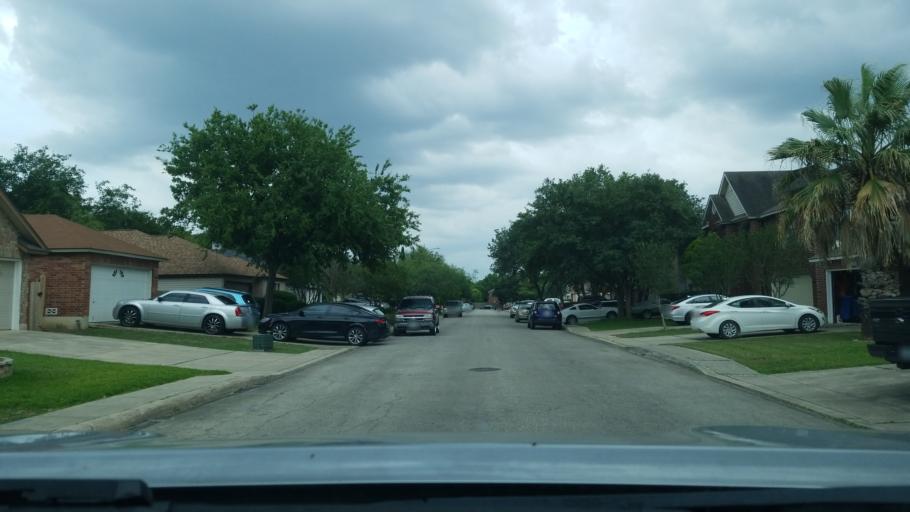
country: US
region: Texas
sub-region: Bexar County
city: Leon Valley
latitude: 29.5403
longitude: -98.6278
